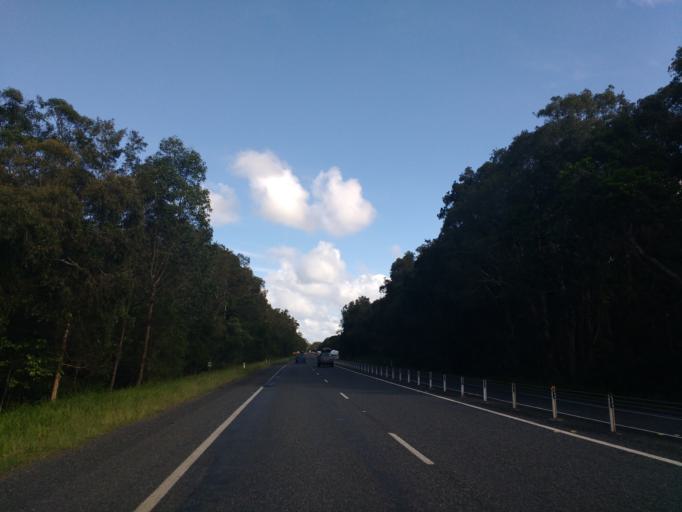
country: AU
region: New South Wales
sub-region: Ballina
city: Ballina
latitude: -28.9103
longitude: 153.4787
